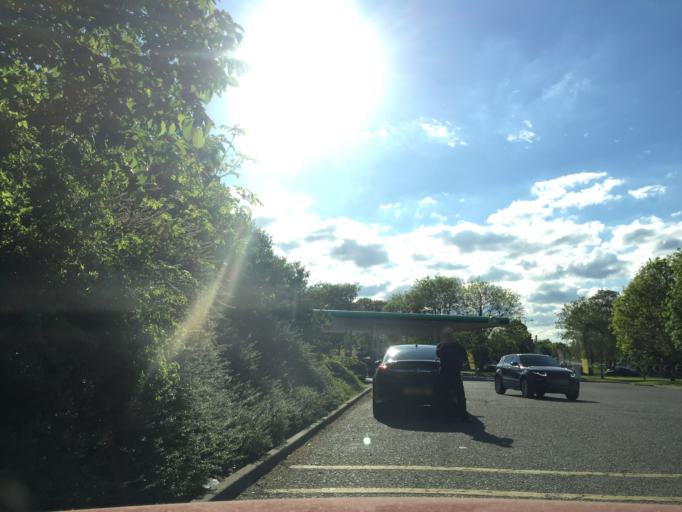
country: GB
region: England
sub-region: Coventry
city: Coventry
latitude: 52.3792
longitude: -1.5144
